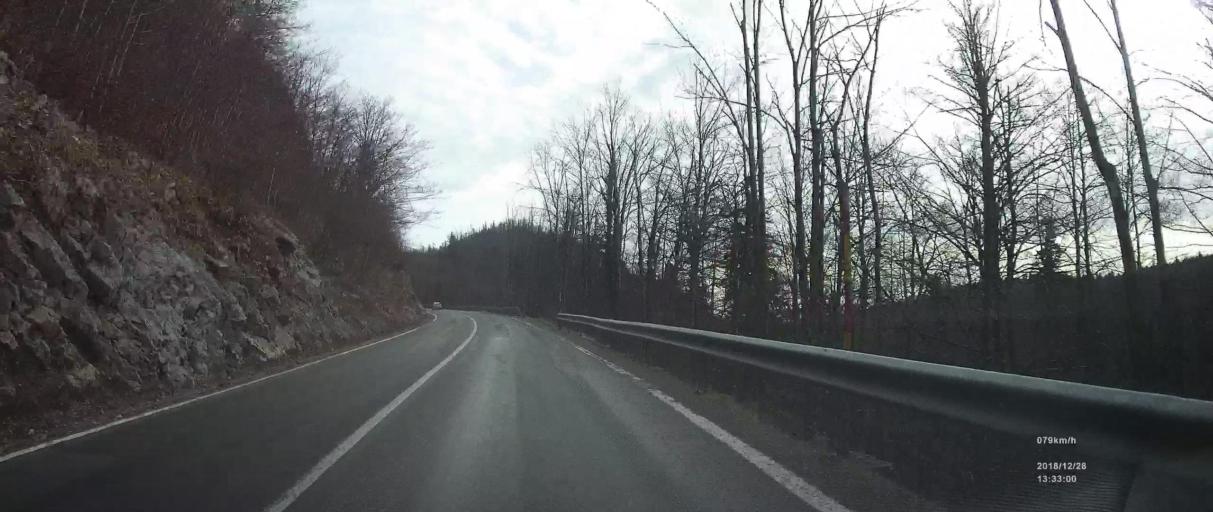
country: HR
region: Primorsko-Goranska
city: Hreljin
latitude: 45.3420
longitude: 14.6714
